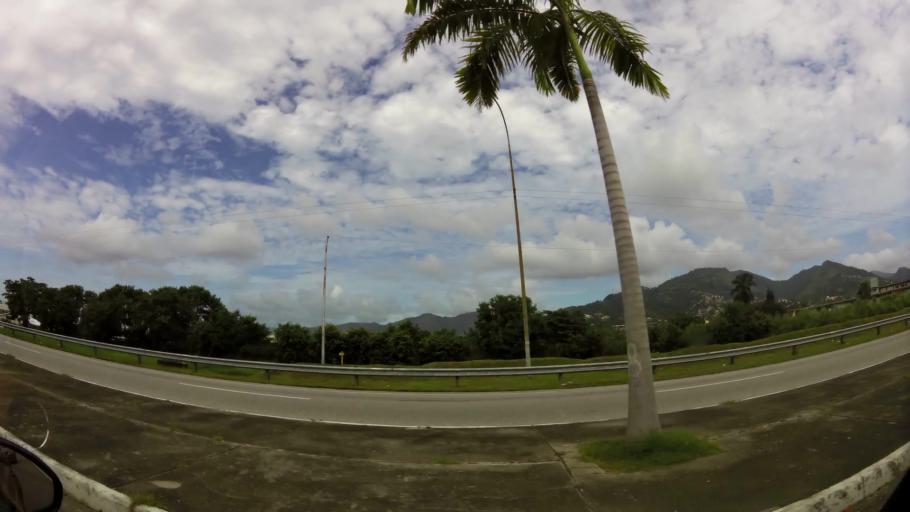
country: TT
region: City of Port of Spain
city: Mucurapo
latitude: 10.6631
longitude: -61.5330
